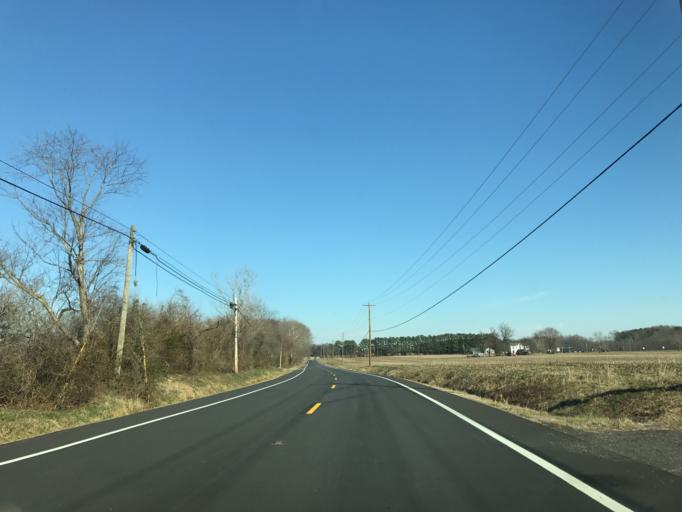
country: US
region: Maryland
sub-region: Queen Anne's County
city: Grasonville
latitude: 38.9916
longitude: -76.1507
